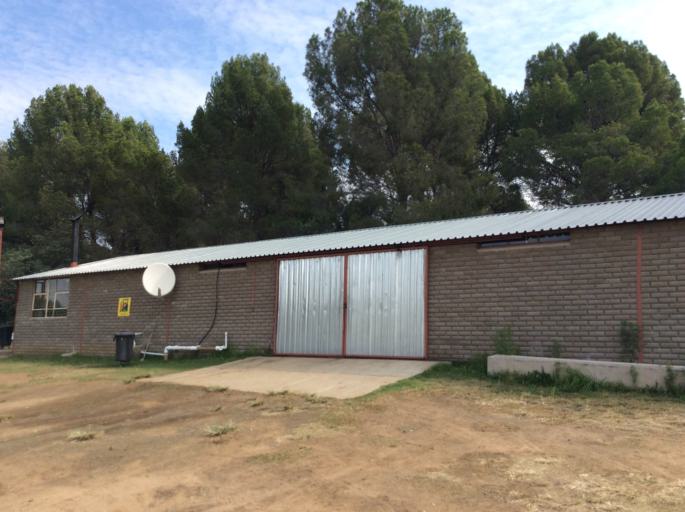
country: ZA
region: Orange Free State
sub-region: Xhariep District Municipality
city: Dewetsdorp
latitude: -29.5753
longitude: 26.6649
